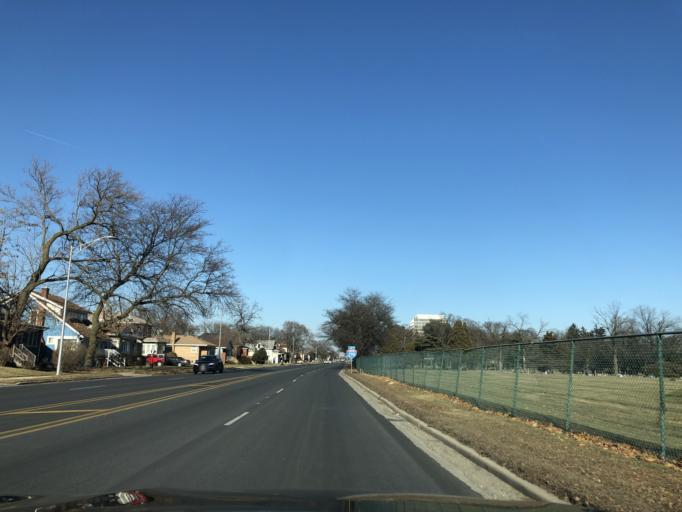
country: US
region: Illinois
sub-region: Cook County
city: Maywood
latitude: 41.8664
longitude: -87.8334
